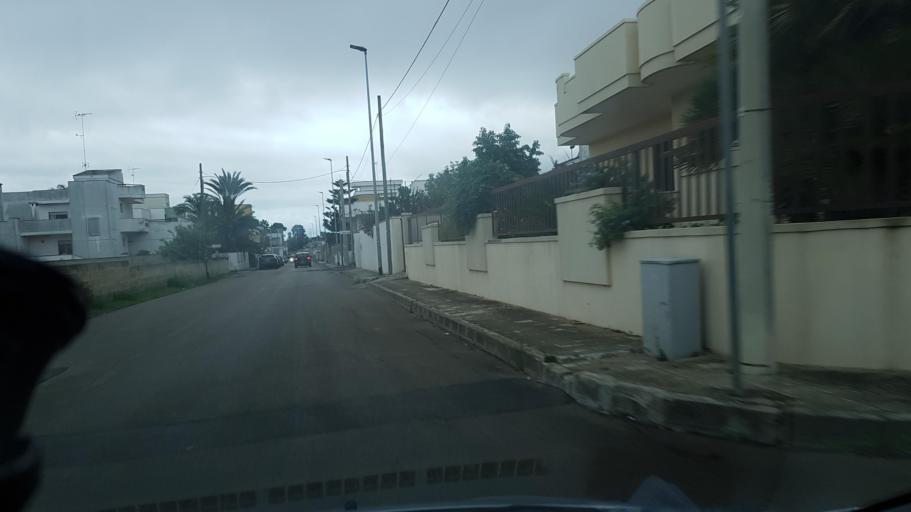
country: IT
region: Apulia
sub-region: Provincia di Lecce
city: Carmiano
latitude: 40.3446
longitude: 18.0397
